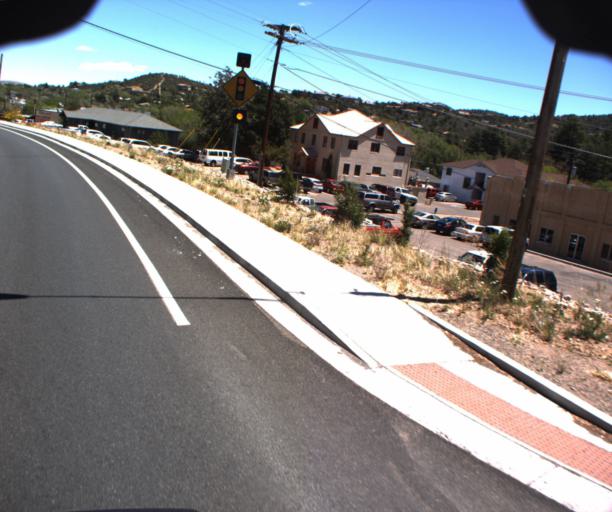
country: US
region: Arizona
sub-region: Yavapai County
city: Prescott
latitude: 34.5285
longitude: -112.4771
